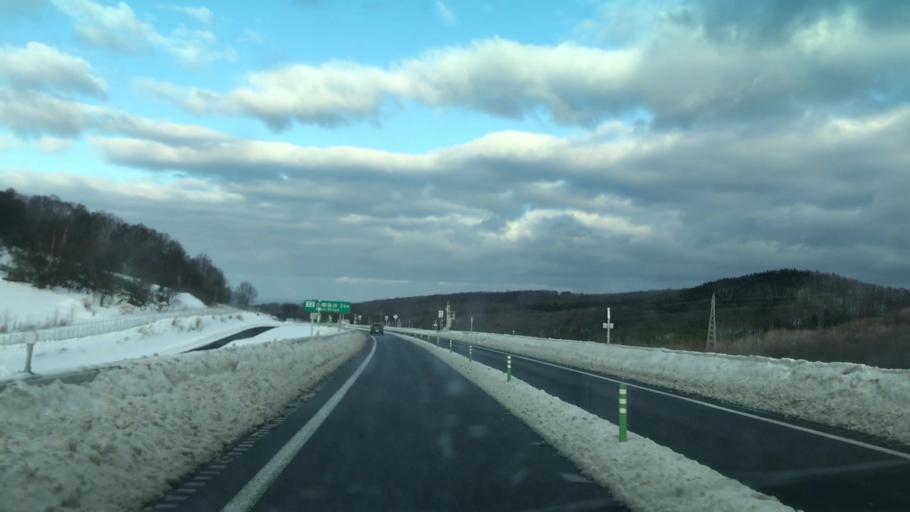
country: JP
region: Hokkaido
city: Otaru
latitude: 43.1955
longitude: 140.9526
